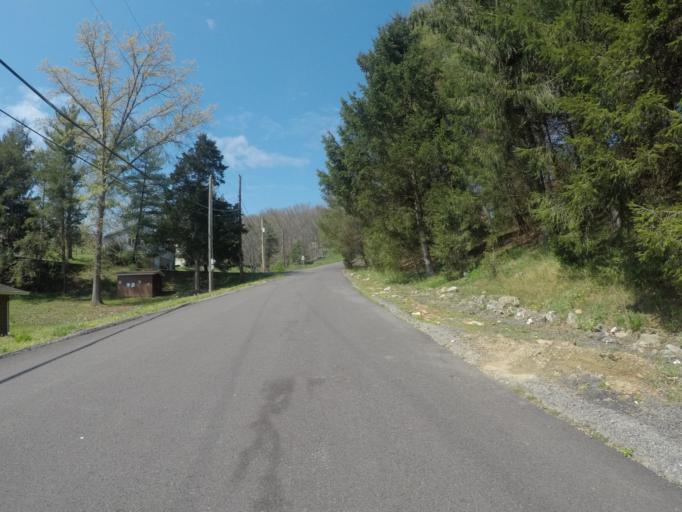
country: US
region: Ohio
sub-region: Lawrence County
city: Burlington
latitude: 38.3795
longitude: -82.5279
